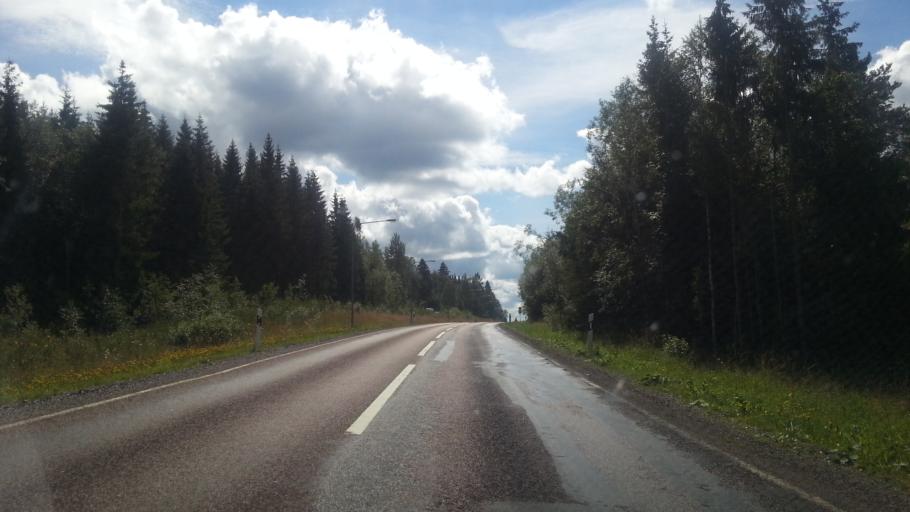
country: SE
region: Dalarna
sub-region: Ludvika Kommun
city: Grangesberg
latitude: 60.0244
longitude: 14.9796
